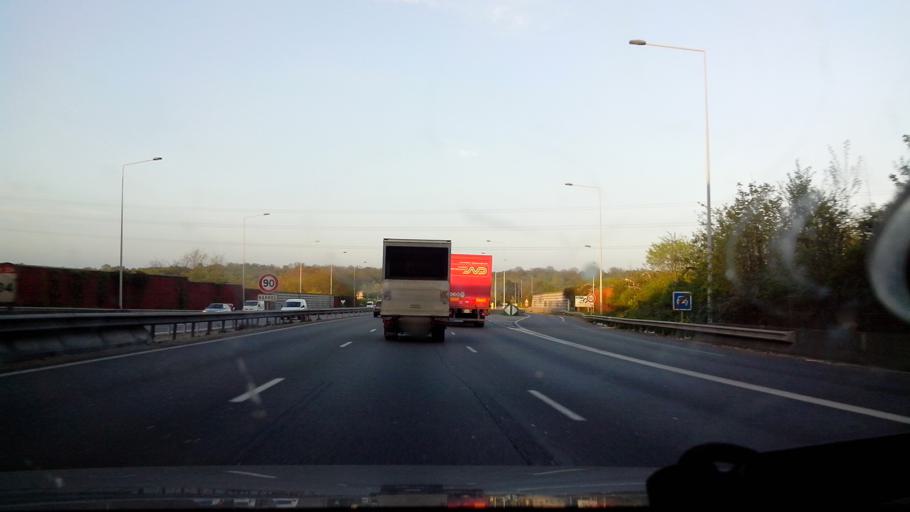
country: FR
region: Ile-de-France
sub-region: Departement de l'Essonne
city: Evry
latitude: 48.6222
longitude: 2.4641
